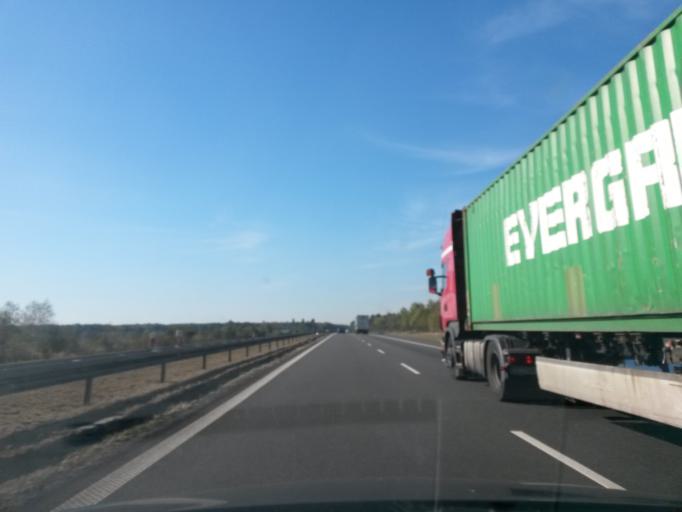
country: PL
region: Opole Voivodeship
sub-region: Powiat opolski
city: Proszkow
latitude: 50.5775
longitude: 17.8424
